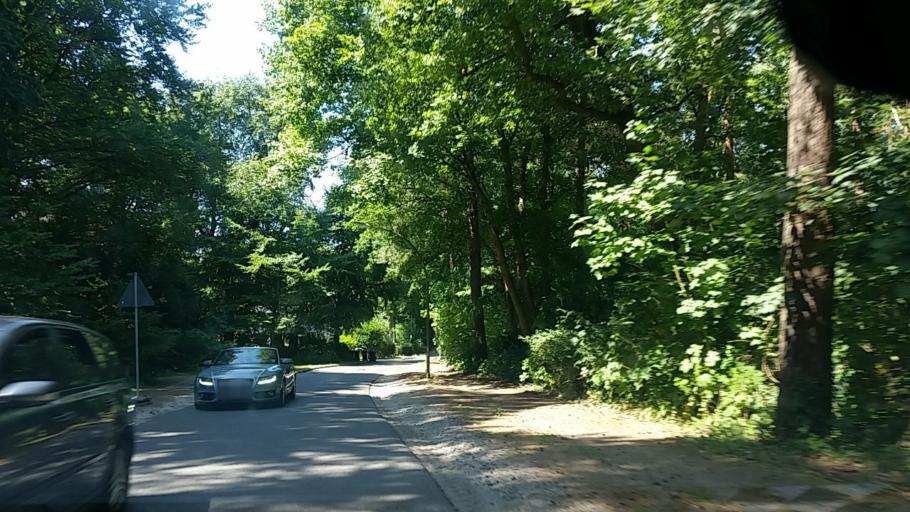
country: DE
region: Schleswig-Holstein
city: Wedel
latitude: 53.5705
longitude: 9.7622
